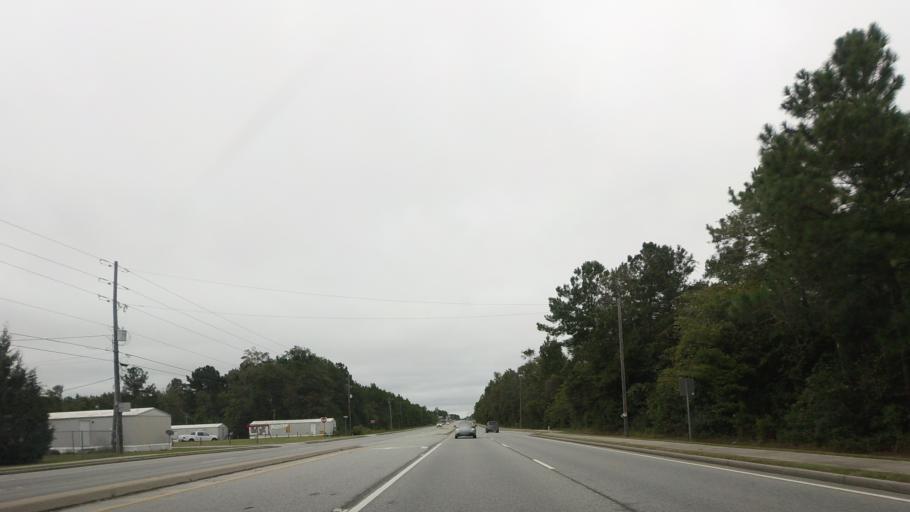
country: US
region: Georgia
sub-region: Berrien County
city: Ray City
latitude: 30.9644
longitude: -83.2196
